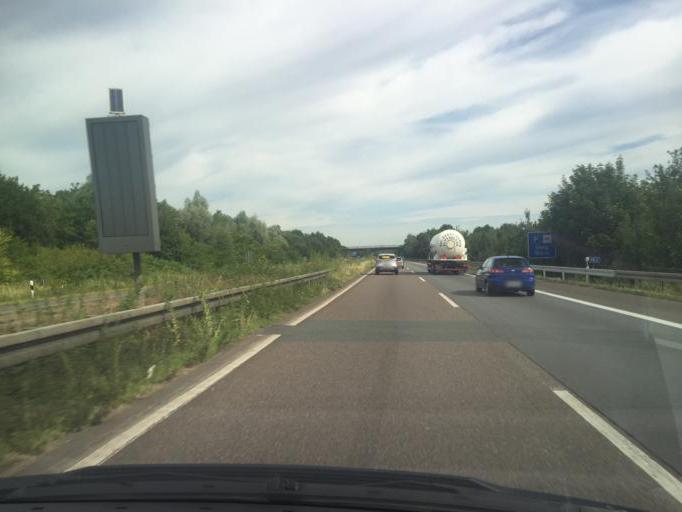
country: DE
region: North Rhine-Westphalia
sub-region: Regierungsbezirk Dusseldorf
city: Moers
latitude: 51.4663
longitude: 6.5901
